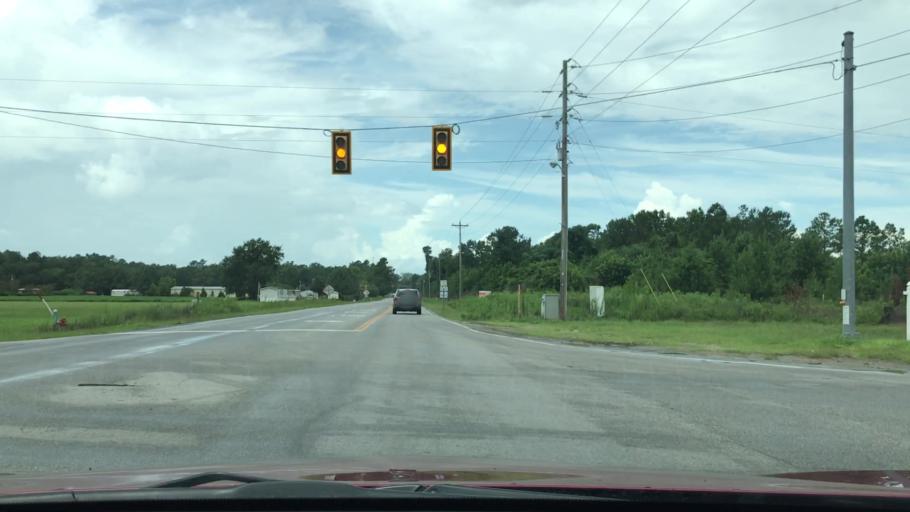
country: US
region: South Carolina
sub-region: Horry County
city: Loris
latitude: 33.9049
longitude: -78.8404
